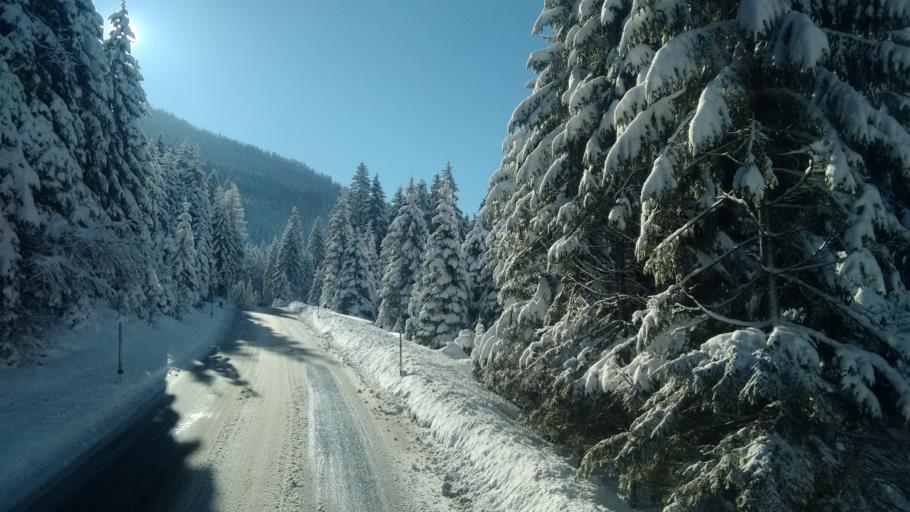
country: AT
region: Salzburg
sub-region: Politischer Bezirk Sankt Johann im Pongau
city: Untertauern
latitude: 47.3053
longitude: 13.4530
